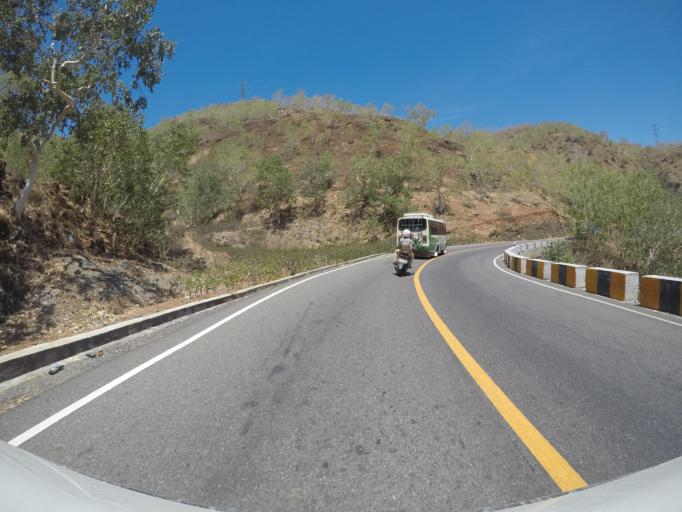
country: TL
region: Manatuto
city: Manatuto
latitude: -8.4775
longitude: 125.9000
